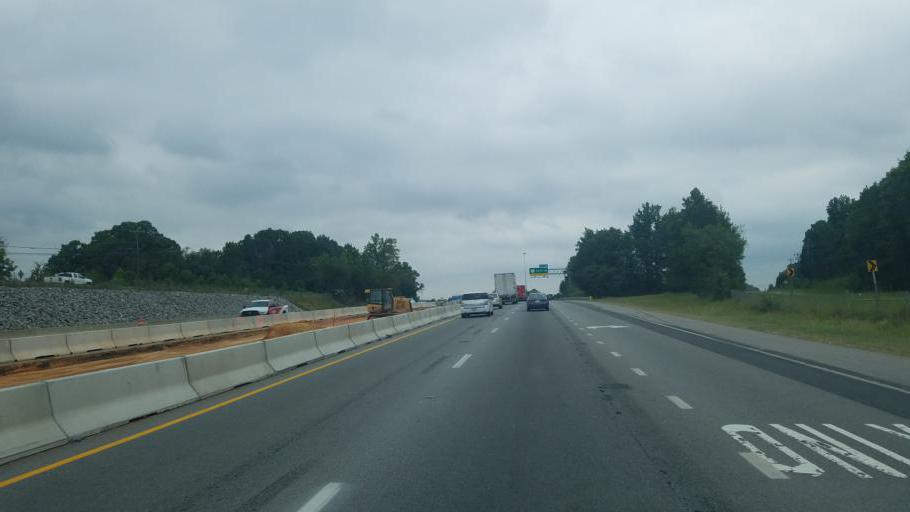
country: US
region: North Carolina
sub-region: Gaston County
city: Davidson
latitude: 35.5483
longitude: -80.8583
